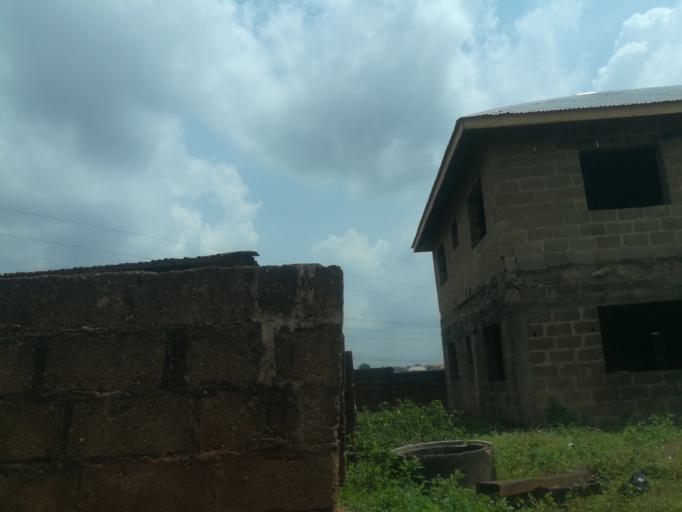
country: NG
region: Oyo
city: Moniya
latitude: 7.4545
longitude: 3.9574
